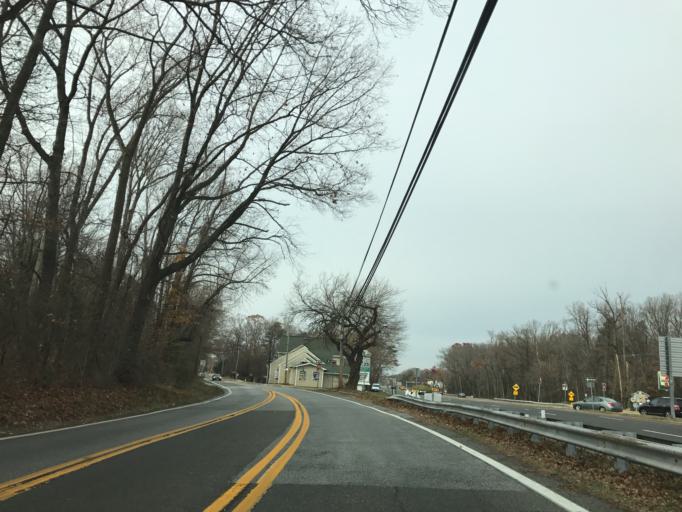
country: US
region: Maryland
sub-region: Anne Arundel County
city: Severna Park
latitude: 39.0542
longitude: -76.5251
